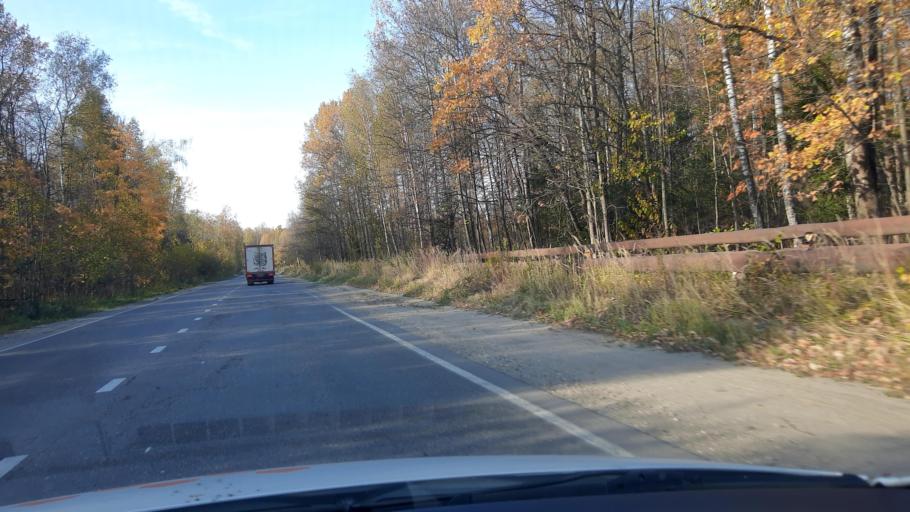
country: RU
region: Moskovskaya
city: Fryazevo
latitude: 55.7687
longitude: 38.4860
